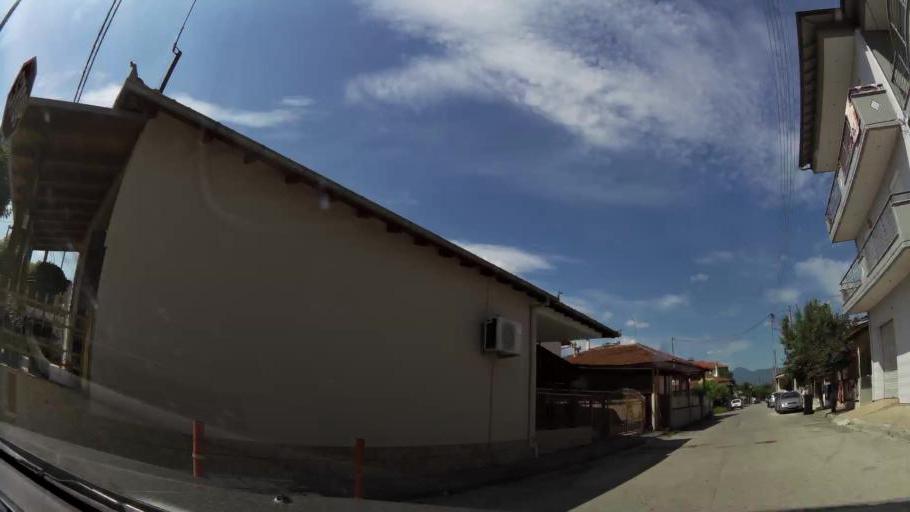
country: GR
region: Central Macedonia
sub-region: Nomos Pierias
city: Katerini
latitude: 40.2630
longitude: 22.4963
